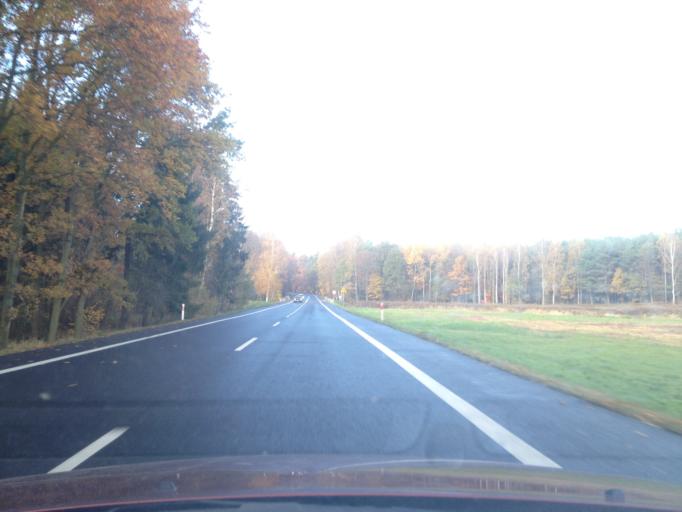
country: PL
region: Lower Silesian Voivodeship
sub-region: Powiat zgorzelecki
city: Lagow
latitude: 51.1557
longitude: 15.0678
